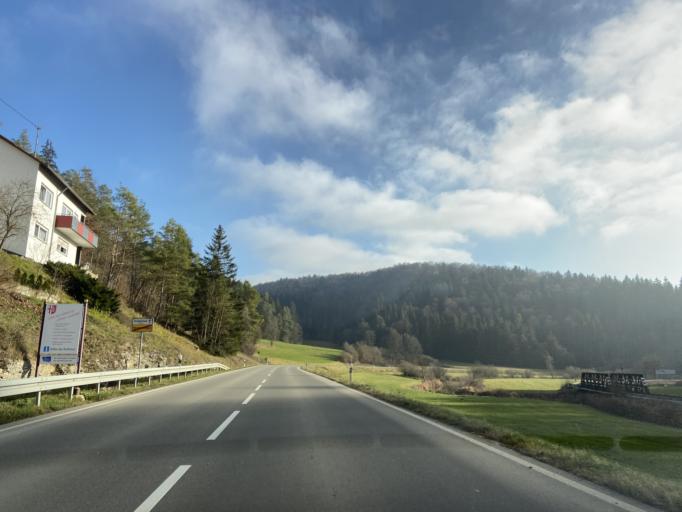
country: DE
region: Baden-Wuerttemberg
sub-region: Tuebingen Region
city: Veringenstadt
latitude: 48.1979
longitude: 9.2189
